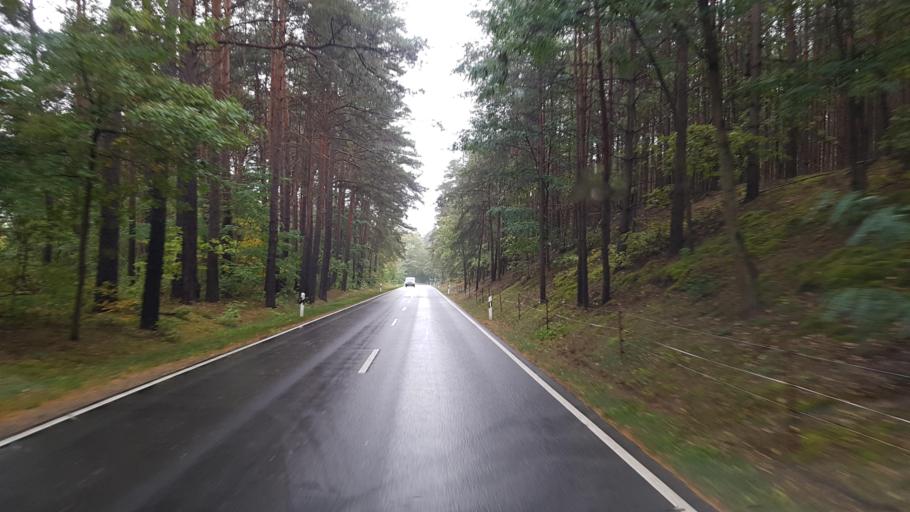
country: DE
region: Brandenburg
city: Bad Saarow
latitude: 52.2976
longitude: 14.0489
